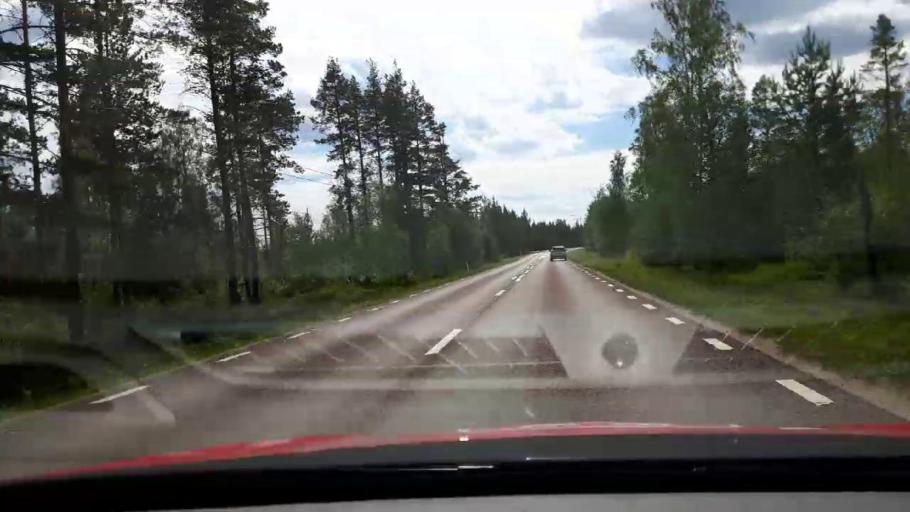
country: SE
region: Jaemtland
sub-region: Harjedalens Kommun
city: Sveg
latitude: 62.1320
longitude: 14.9712
